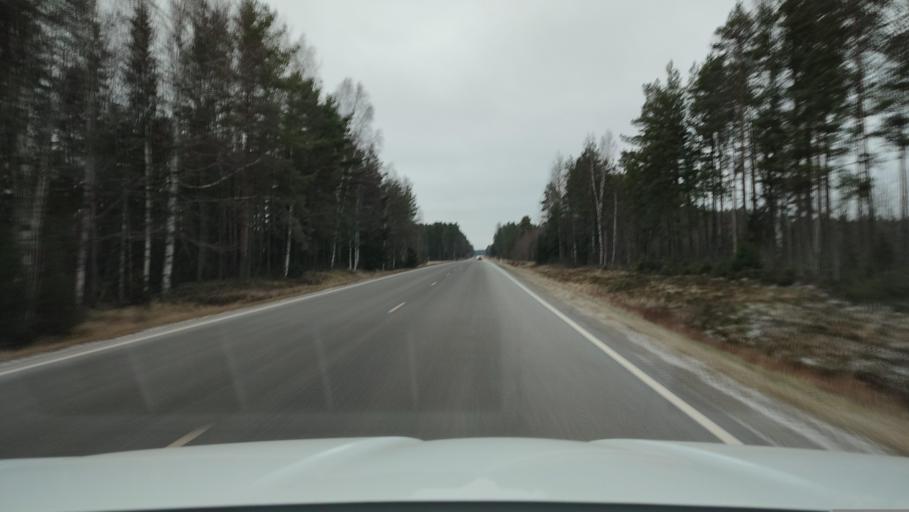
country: FI
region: Ostrobothnia
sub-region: Sydosterbotten
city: Naerpes
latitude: 62.5275
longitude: 21.4609
